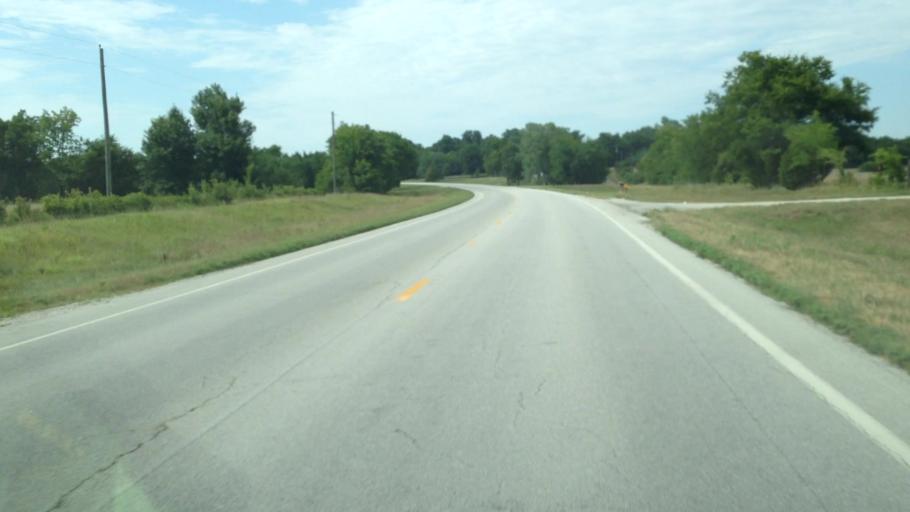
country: US
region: Kansas
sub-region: Labette County
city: Oswego
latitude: 37.1449
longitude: -95.1036
